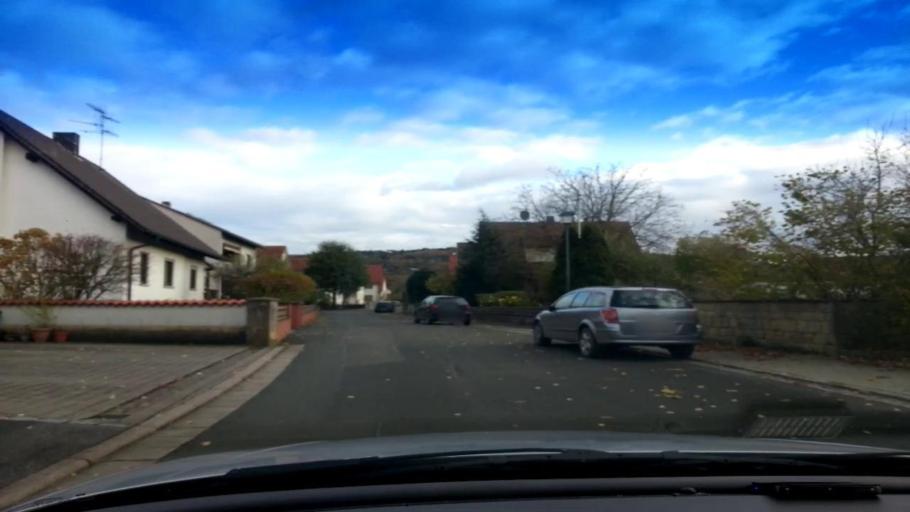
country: DE
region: Bavaria
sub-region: Upper Franconia
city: Rattelsdorf
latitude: 50.0080
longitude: 10.9070
